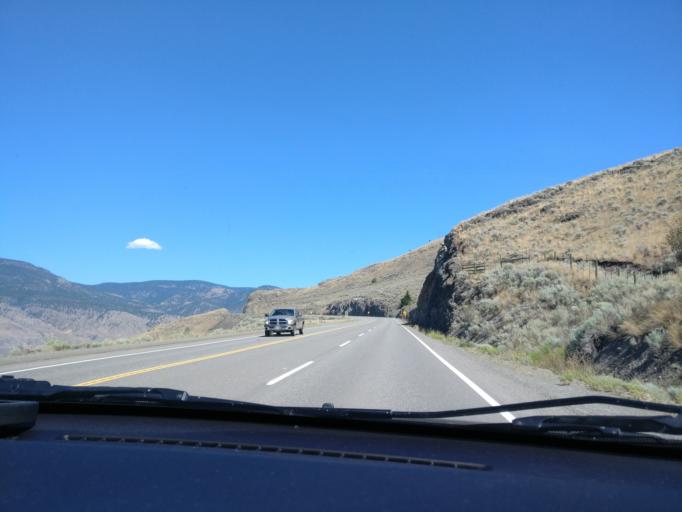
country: CA
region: British Columbia
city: Logan Lake
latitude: 50.7644
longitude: -120.7834
